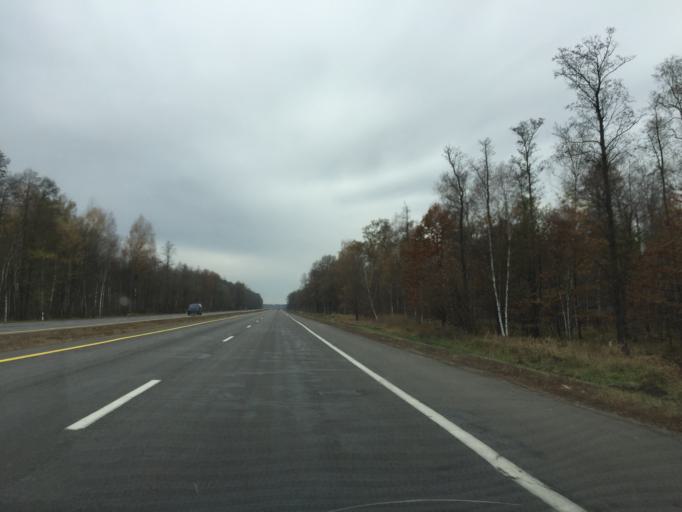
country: BY
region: Gomel
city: Horad Rechytsa
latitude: 52.3518
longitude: 30.5978
